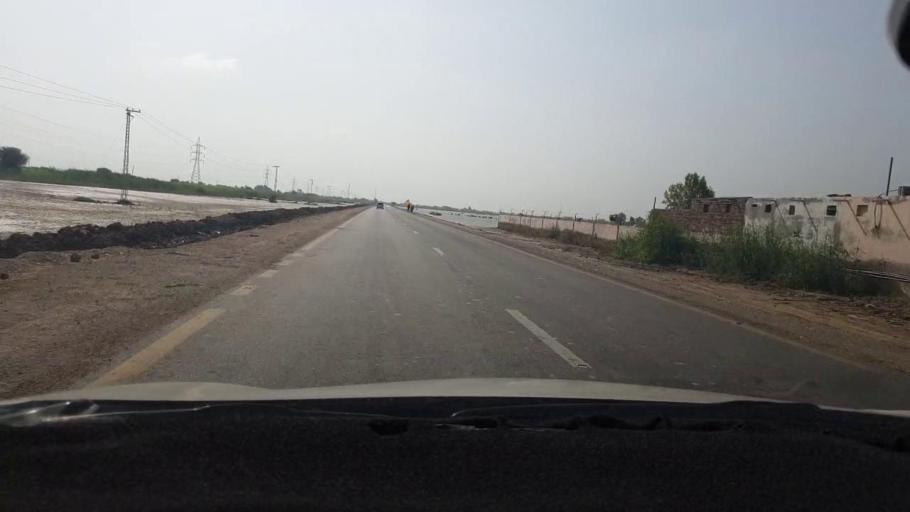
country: PK
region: Sindh
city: Jhol
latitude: 25.8989
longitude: 69.0237
